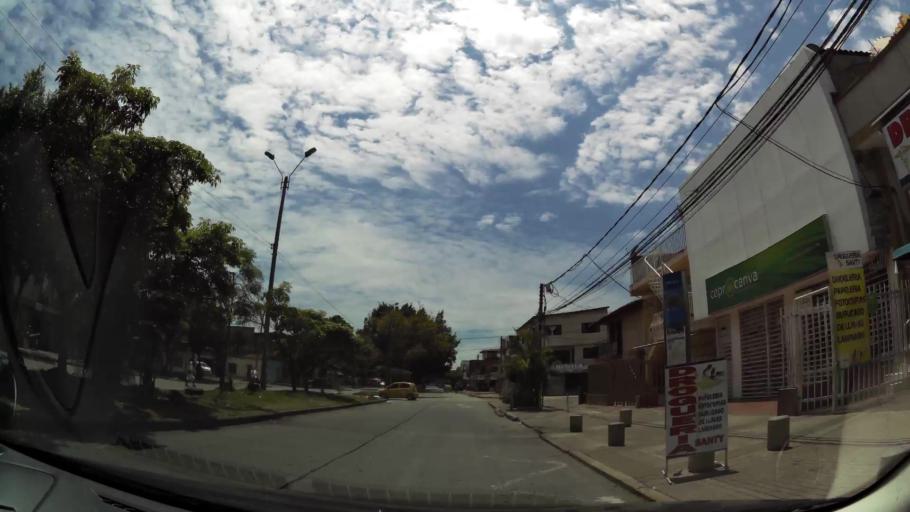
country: CO
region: Valle del Cauca
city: Cali
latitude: 3.4437
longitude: -76.5029
